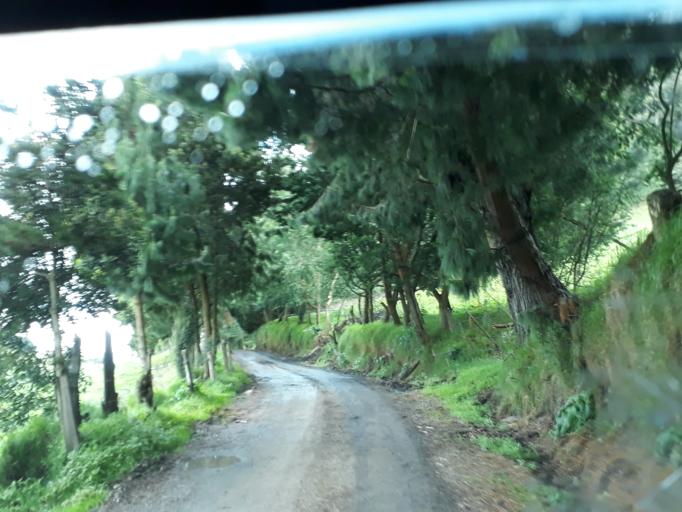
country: CO
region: Cundinamarca
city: La Mesa
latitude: 5.1822
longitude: -73.9072
